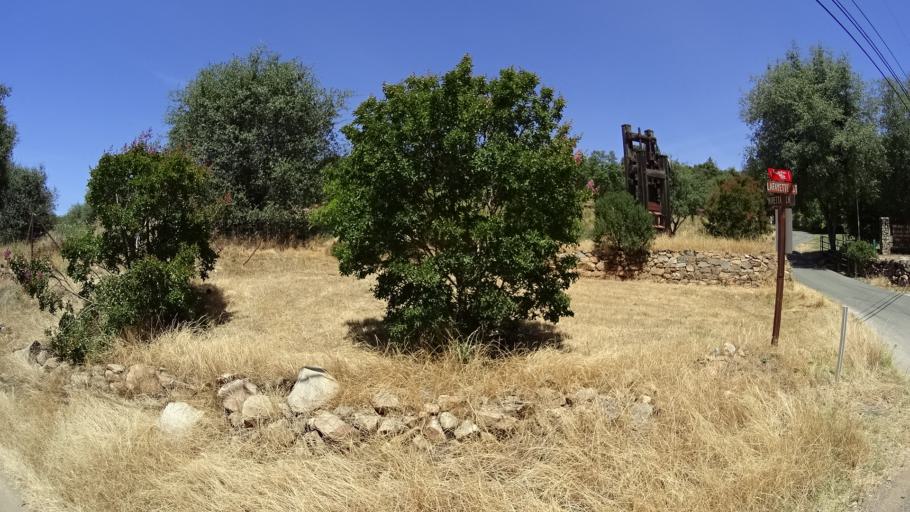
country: US
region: California
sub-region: Amador County
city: Jackson
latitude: 38.2995
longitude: -120.7003
